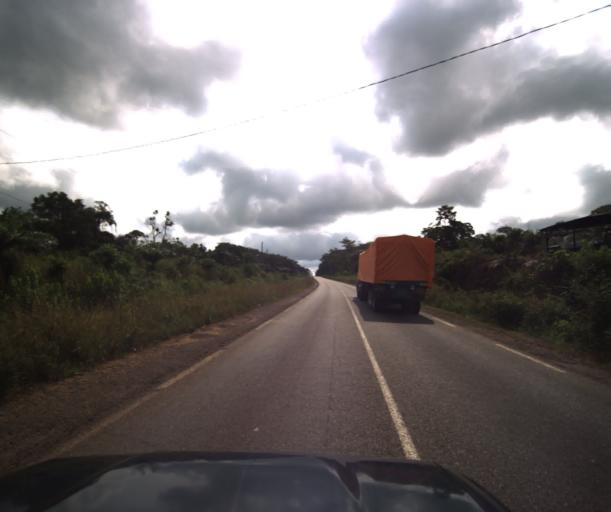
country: CM
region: Littoral
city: Edea
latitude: 3.8065
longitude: 10.2634
